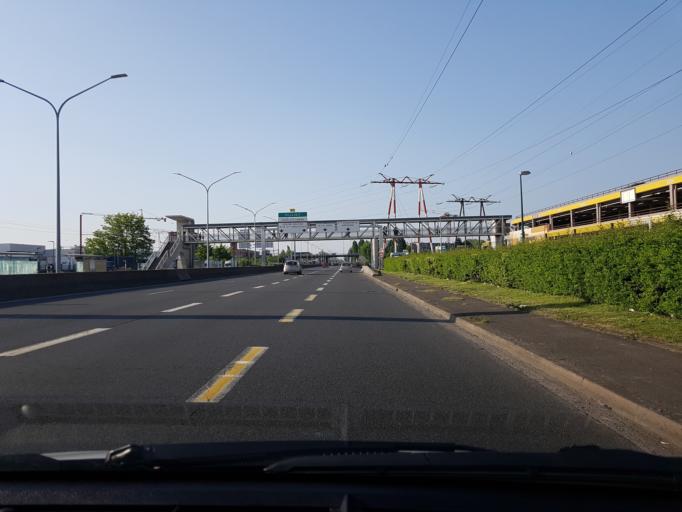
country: FR
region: Ile-de-France
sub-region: Departement du Val-de-Marne
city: Rungis
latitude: 48.7563
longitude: 2.3688
